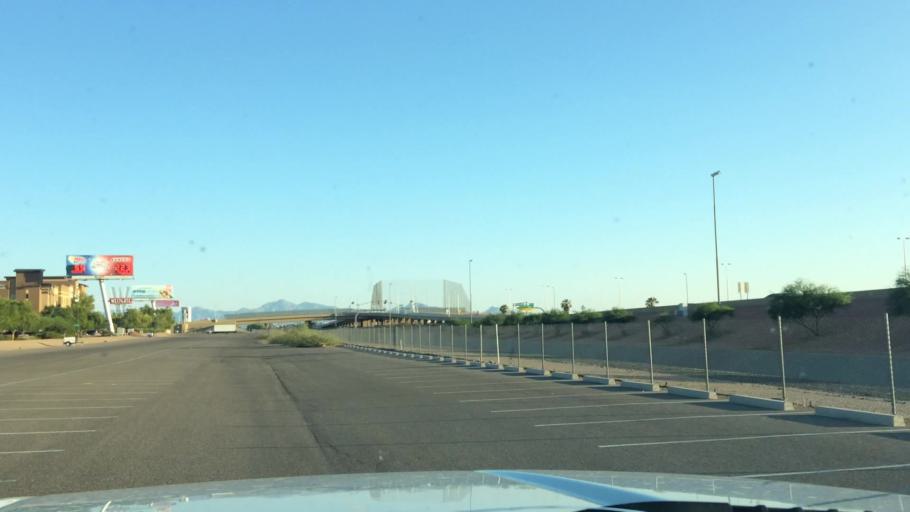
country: US
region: Arizona
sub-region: Maricopa County
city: Peoria
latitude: 33.5343
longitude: -112.2685
